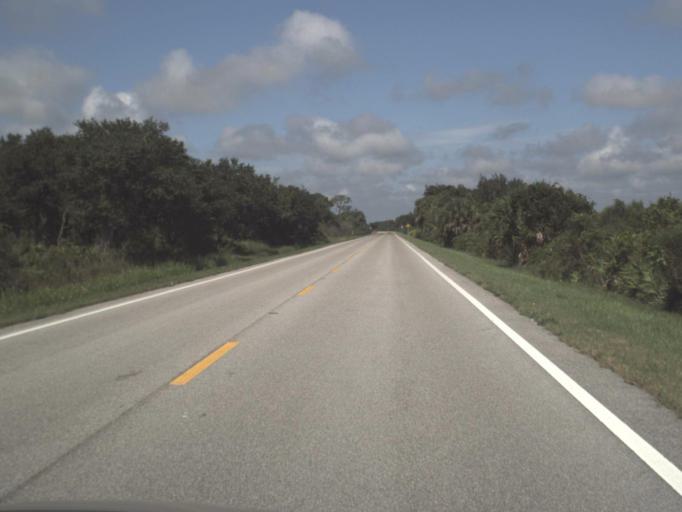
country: US
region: Florida
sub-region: Sarasota County
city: Warm Mineral Springs
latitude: 27.2130
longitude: -82.2625
